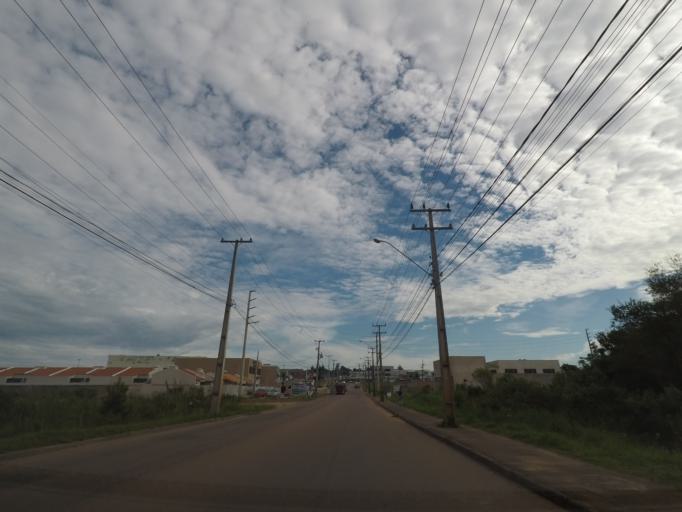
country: BR
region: Parana
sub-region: Araucaria
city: Araucaria
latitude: -25.6390
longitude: -49.3009
